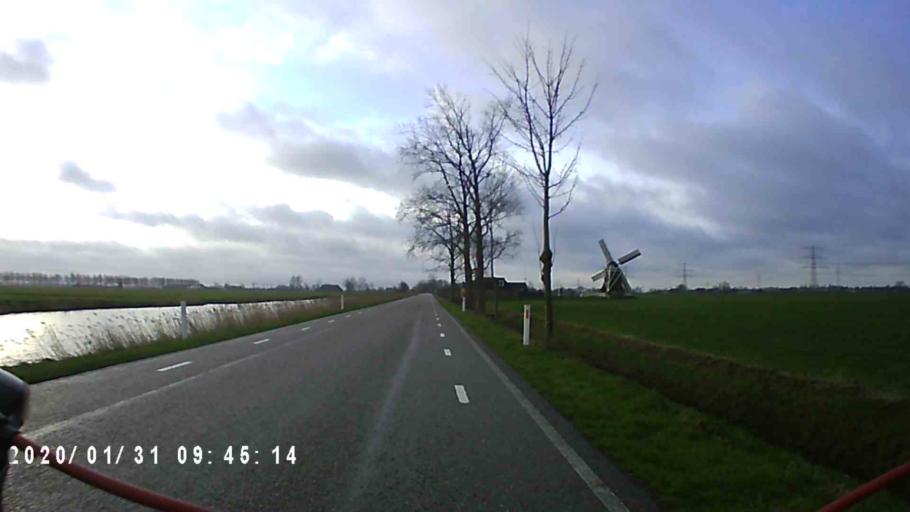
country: NL
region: Groningen
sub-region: Gemeente Zuidhorn
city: Aduard
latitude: 53.2699
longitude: 6.4836
